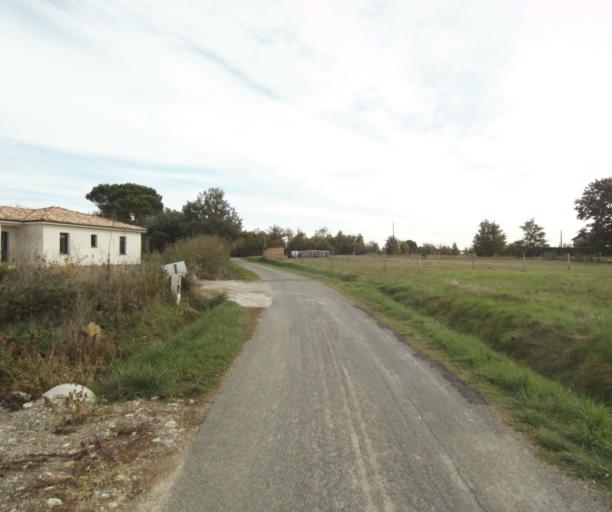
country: FR
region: Midi-Pyrenees
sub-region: Departement de la Haute-Garonne
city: Fronton
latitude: 43.8711
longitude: 1.3865
